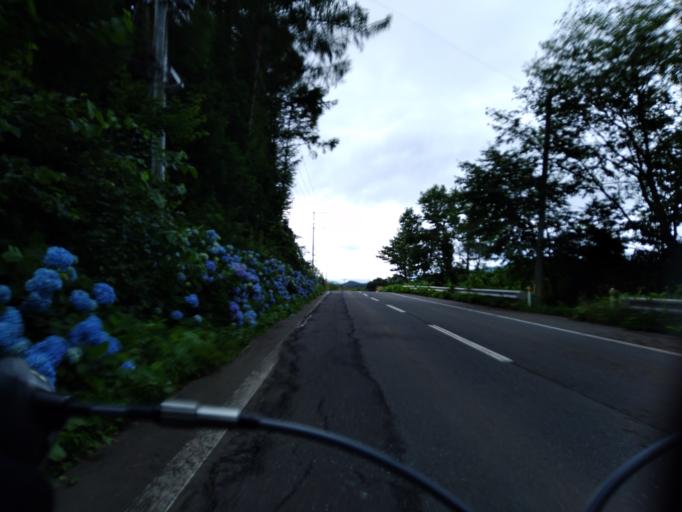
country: JP
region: Iwate
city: Morioka-shi
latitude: 39.8041
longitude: 141.0900
